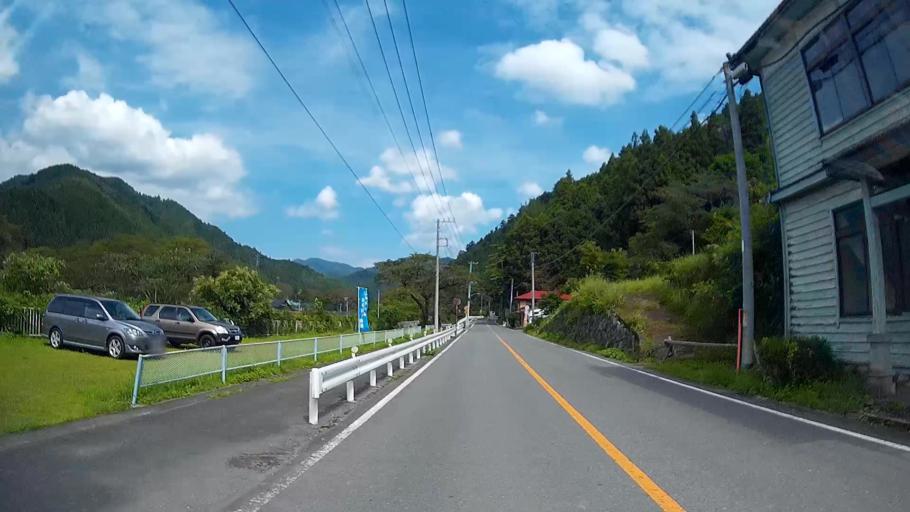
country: JP
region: Tokyo
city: Ome
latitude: 35.8843
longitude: 139.1831
